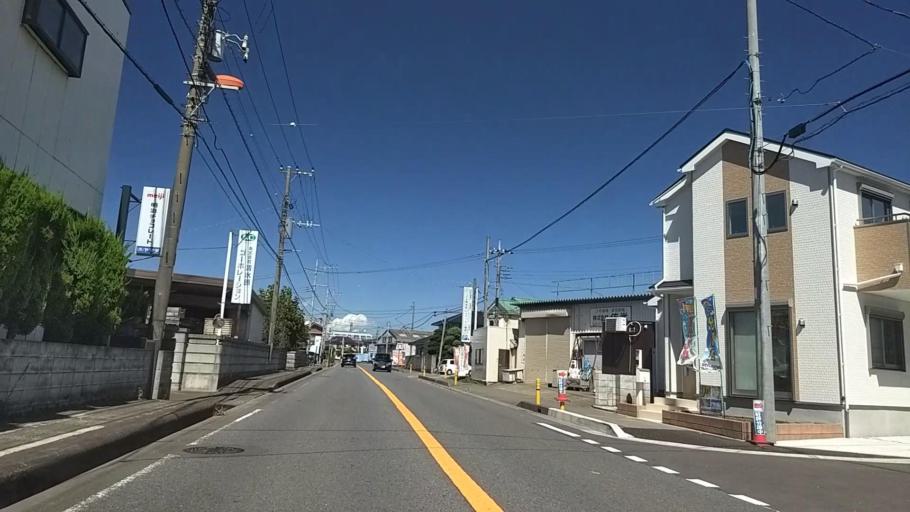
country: JP
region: Tokyo
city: Hachioji
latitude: 35.5611
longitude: 139.3268
